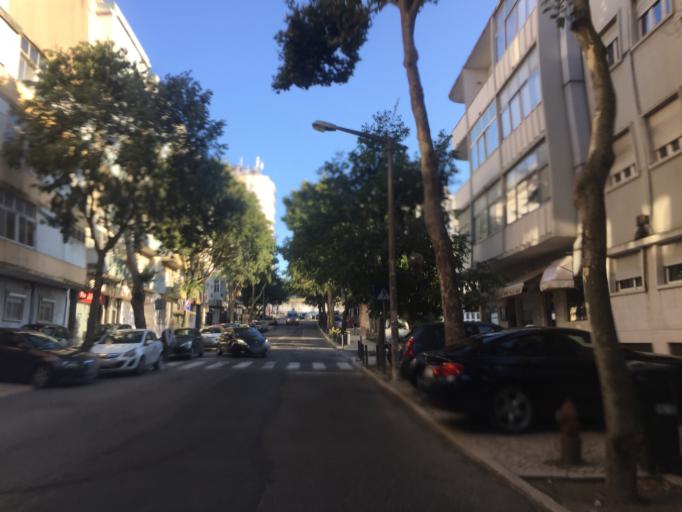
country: PT
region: Lisbon
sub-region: Odivelas
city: Pontinha
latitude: 38.7461
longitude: -9.1980
